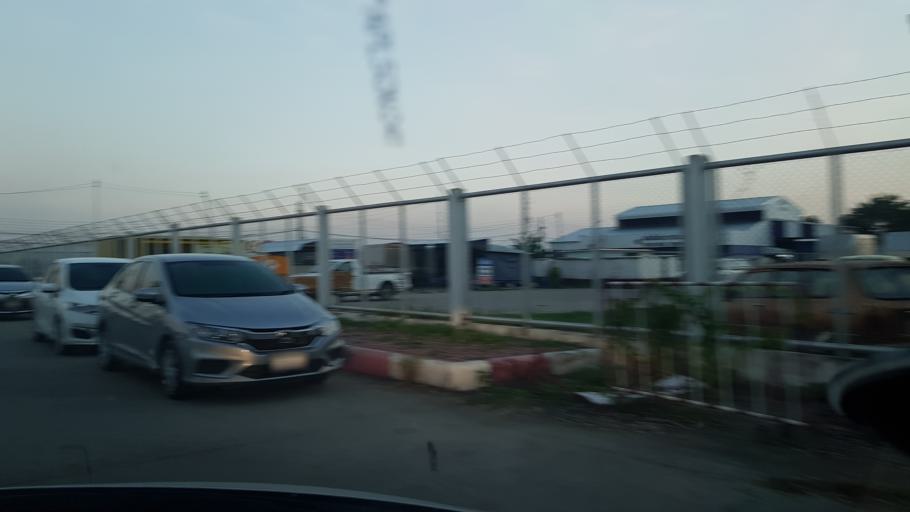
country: TH
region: Chiang Rai
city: Chiang Rai
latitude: 19.9533
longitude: 99.8779
